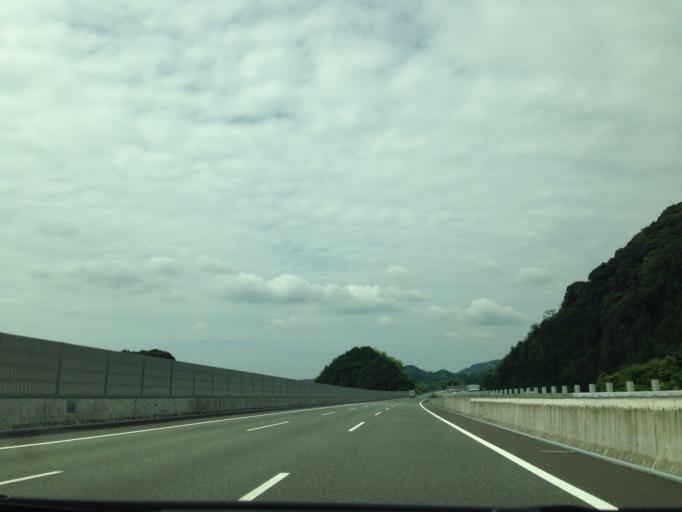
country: JP
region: Shizuoka
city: Fujieda
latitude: 34.9264
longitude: 138.2725
